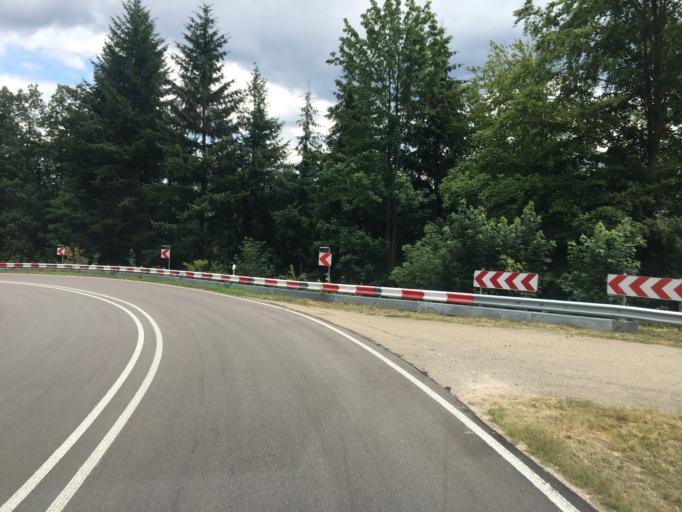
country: DE
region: Baden-Wuerttemberg
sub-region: Karlsruhe Region
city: Baden-Baden
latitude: 48.7117
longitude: 8.2387
